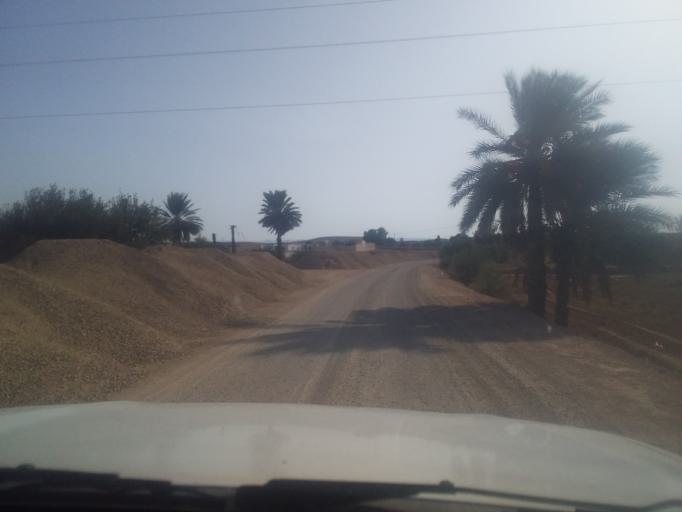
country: TN
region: Qabis
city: Matmata
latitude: 33.5864
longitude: 10.2695
